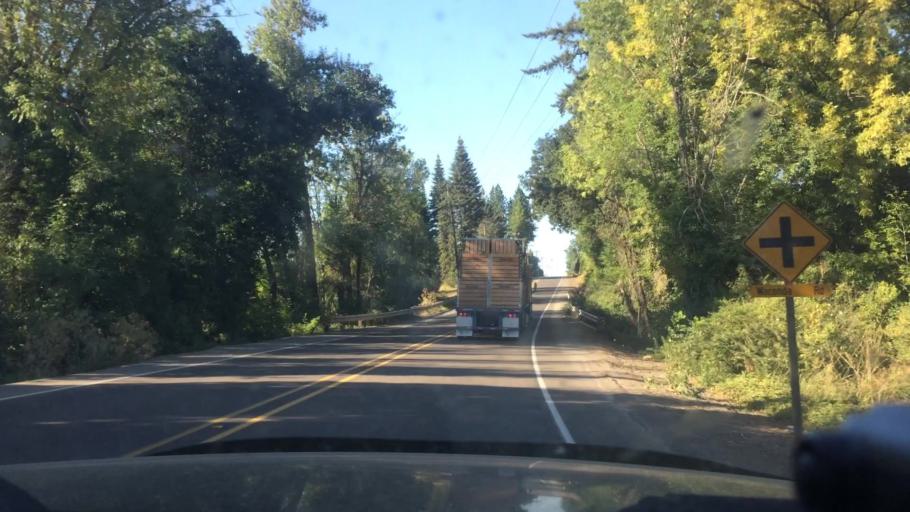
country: US
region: Oregon
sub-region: Marion County
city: Hayesville
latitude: 45.0717
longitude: -122.9793
